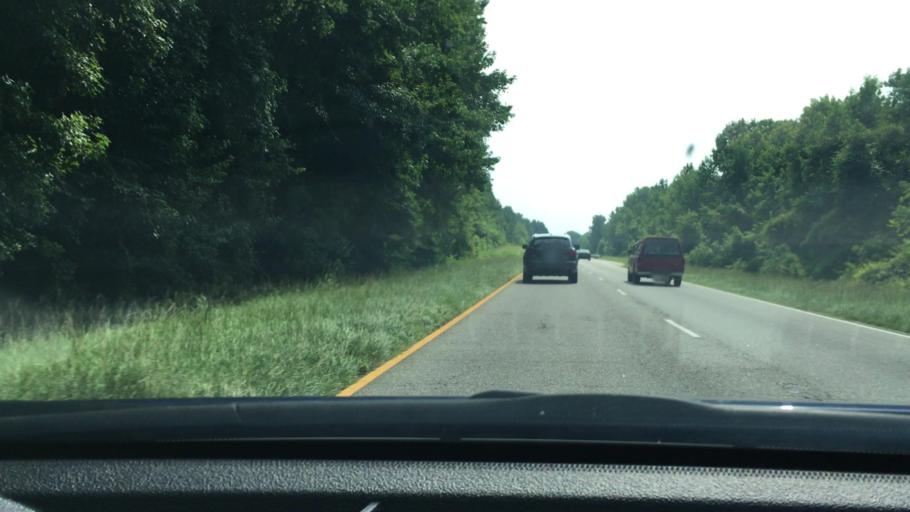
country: US
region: South Carolina
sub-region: Sumter County
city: Stateburg
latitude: 33.9484
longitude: -80.6131
